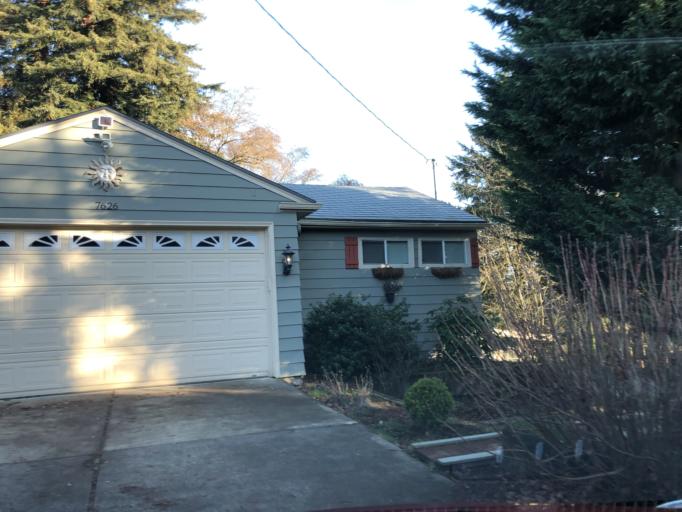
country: US
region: Oregon
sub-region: Clackamas County
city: Milwaukie
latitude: 45.4689
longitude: -122.6775
